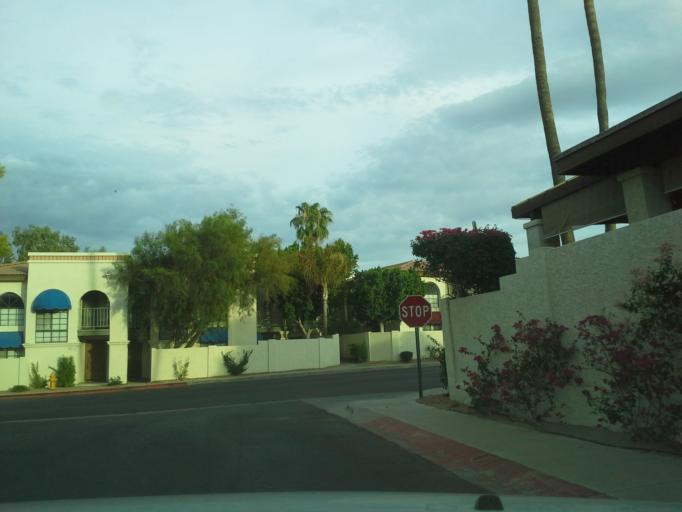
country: US
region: Arizona
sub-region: Maricopa County
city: Guadalupe
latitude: 33.3657
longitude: -111.9748
